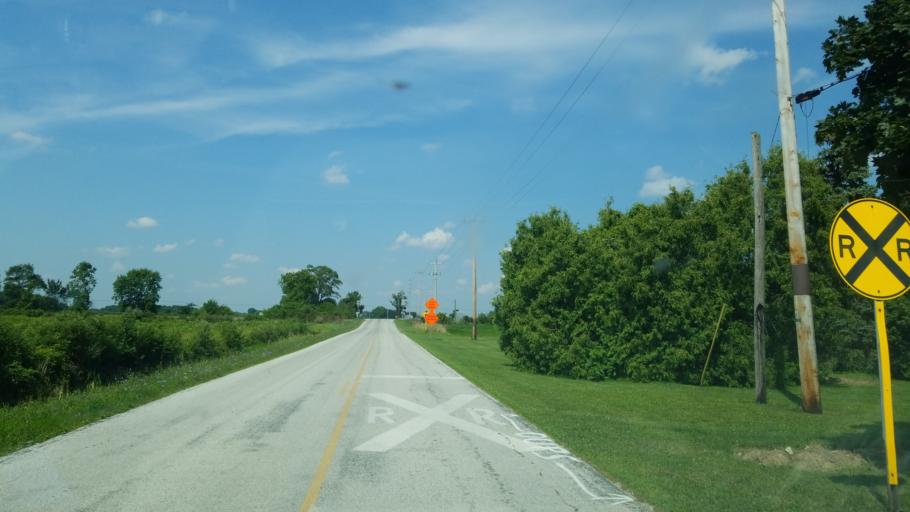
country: US
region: Ohio
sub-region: Seneca County
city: Fostoria
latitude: 41.2179
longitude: -83.4175
